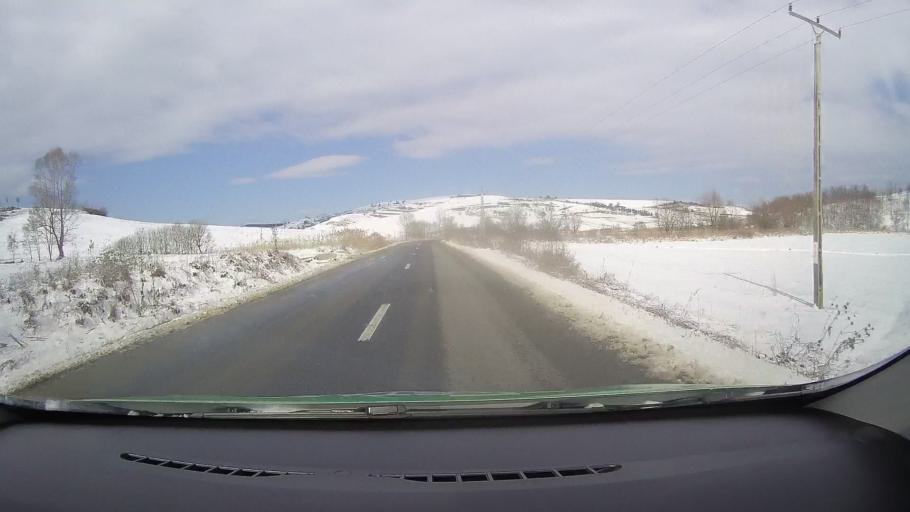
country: RO
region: Sibiu
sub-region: Comuna Altina
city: Altina
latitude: 45.9737
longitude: 24.4660
